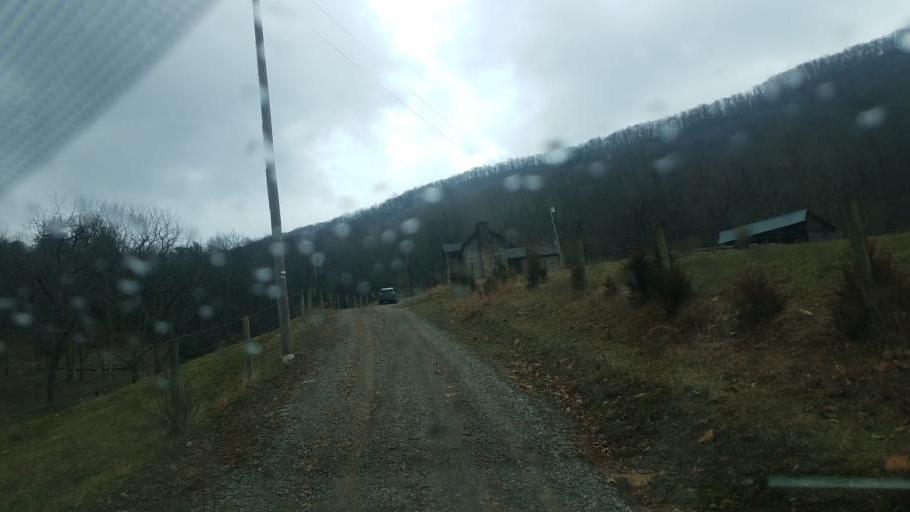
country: US
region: Virginia
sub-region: Pulaski County
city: Dublin
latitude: 37.2176
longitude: -80.7001
